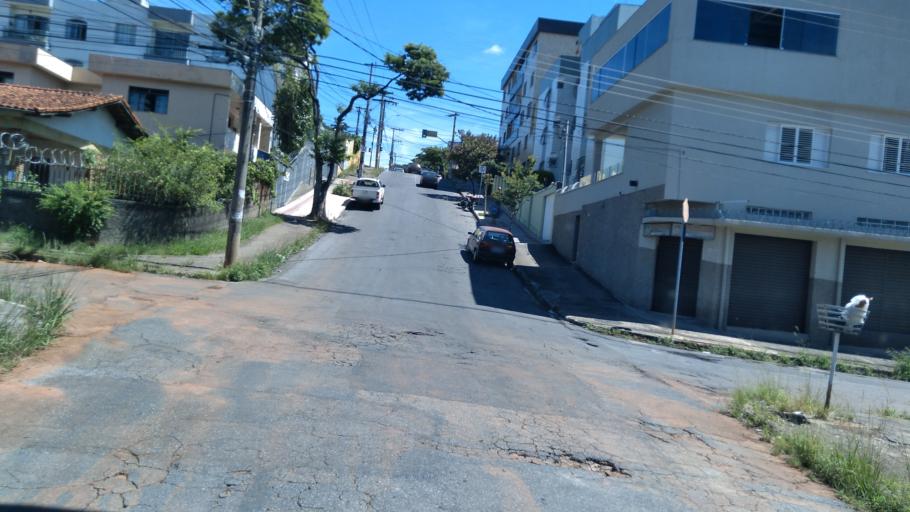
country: BR
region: Minas Gerais
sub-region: Belo Horizonte
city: Belo Horizonte
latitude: -19.9159
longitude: -43.9883
